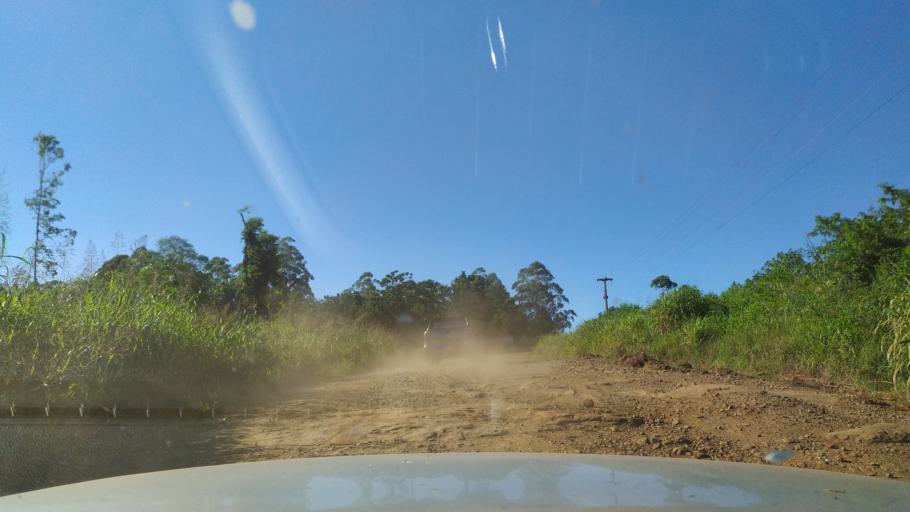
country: AR
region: Misiones
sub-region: Departamento de Montecarlo
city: Montecarlo
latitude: -26.6203
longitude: -54.6962
